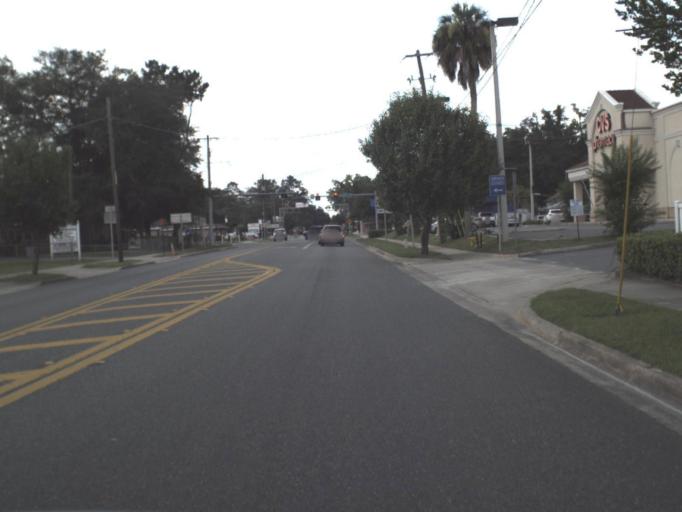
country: US
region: Florida
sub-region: Baker County
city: Macclenny
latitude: 30.2834
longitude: -82.1240
